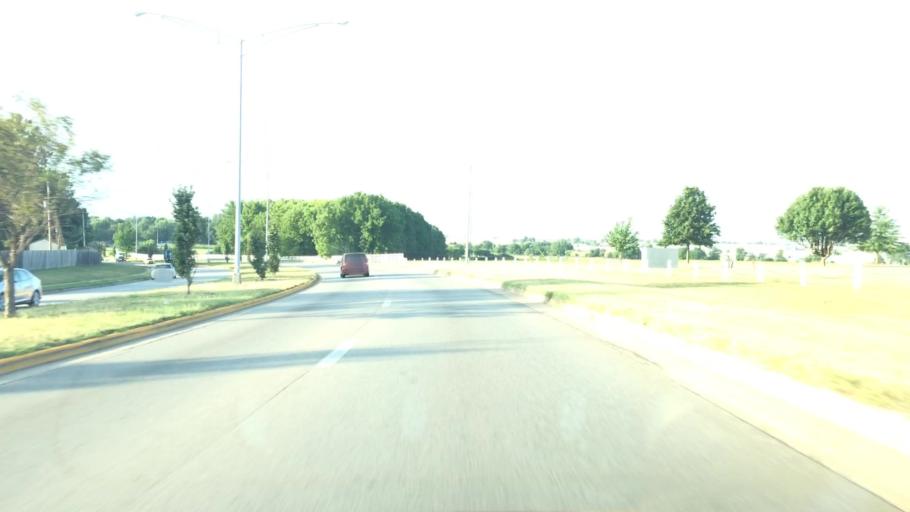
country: US
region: Missouri
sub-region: Greene County
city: Springfield
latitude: 37.1770
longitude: -93.3182
